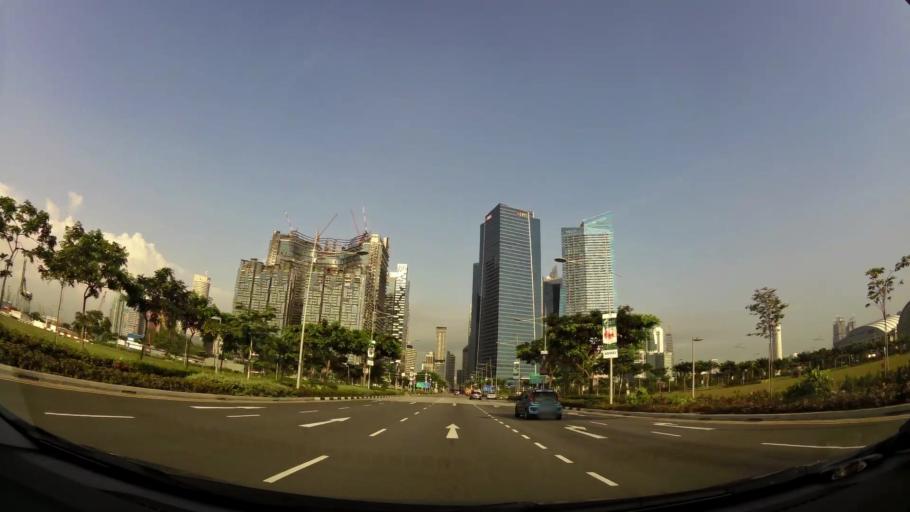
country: SG
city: Singapore
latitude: 1.2761
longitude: 103.8582
